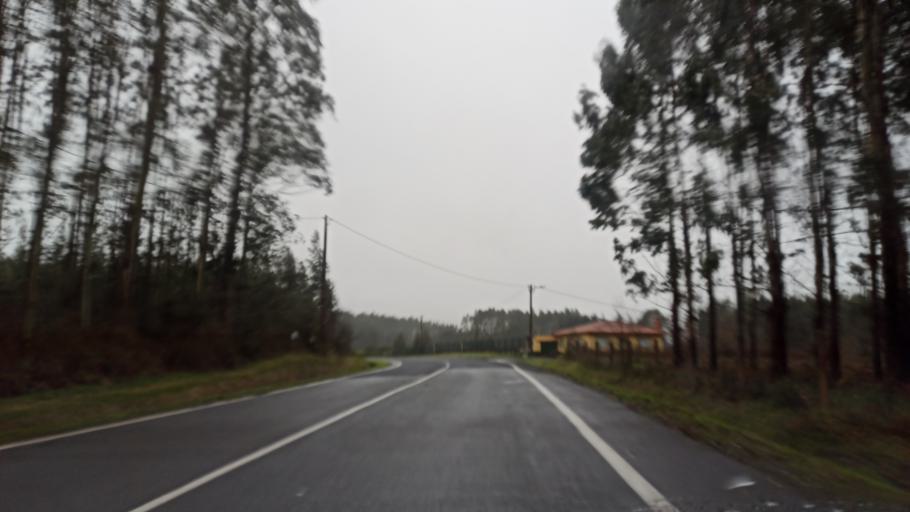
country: ES
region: Galicia
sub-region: Provincia da Coruna
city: Coiros
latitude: 43.1811
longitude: -8.1228
